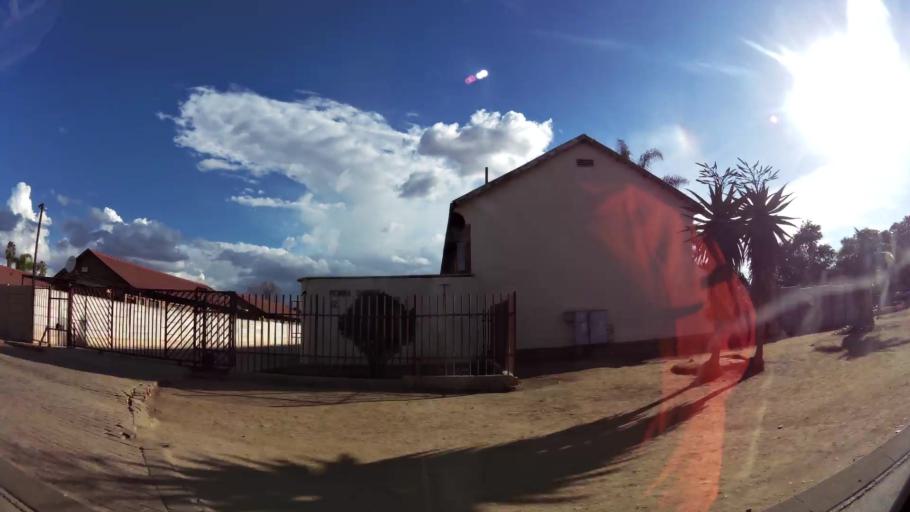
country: ZA
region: Limpopo
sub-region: Capricorn District Municipality
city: Polokwane
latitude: -23.9312
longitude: 29.4525
